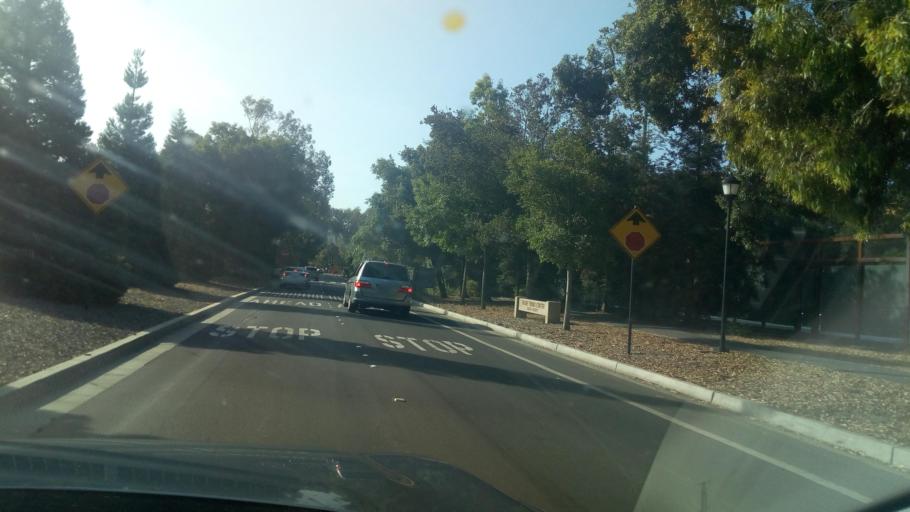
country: US
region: California
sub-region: Santa Clara County
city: Stanford
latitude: 37.4300
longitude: -122.1625
